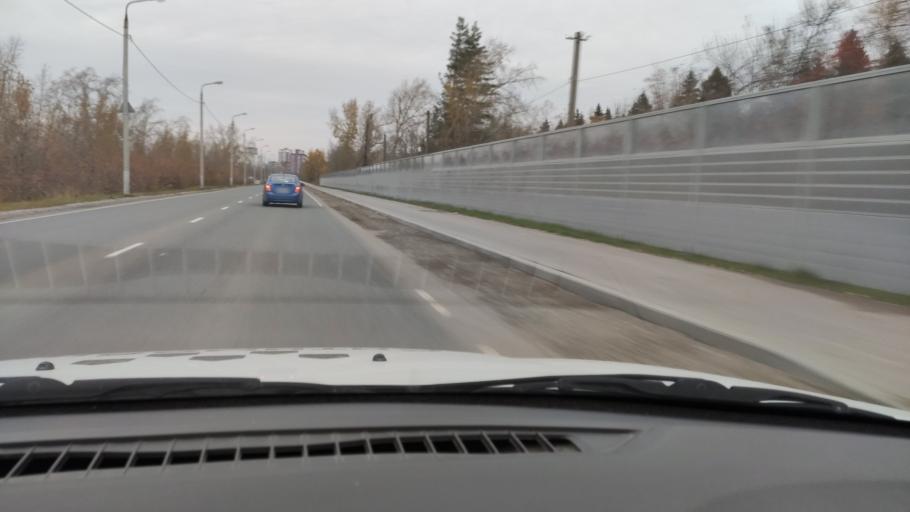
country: RU
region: Perm
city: Kondratovo
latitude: 57.9807
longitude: 56.1313
